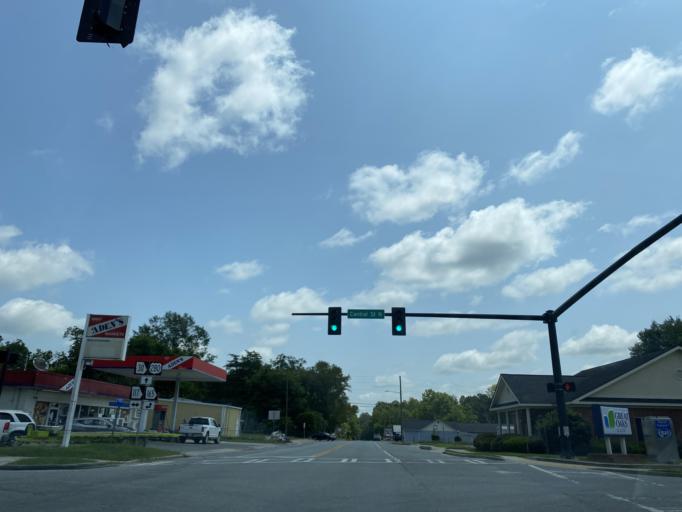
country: US
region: Georgia
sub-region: Wilcox County
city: Abbeville
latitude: 31.9898
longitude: -83.2002
